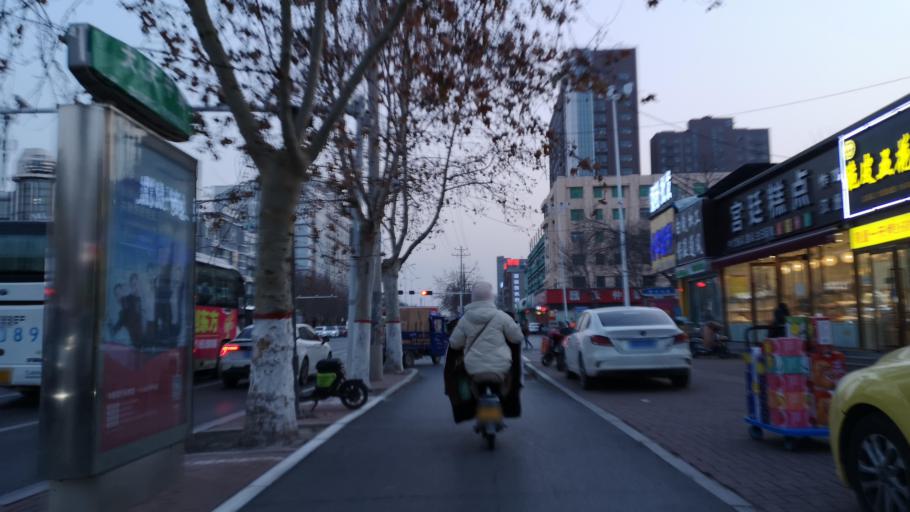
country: CN
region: Henan Sheng
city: Zhongyuanlu
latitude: 35.7696
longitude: 115.0691
